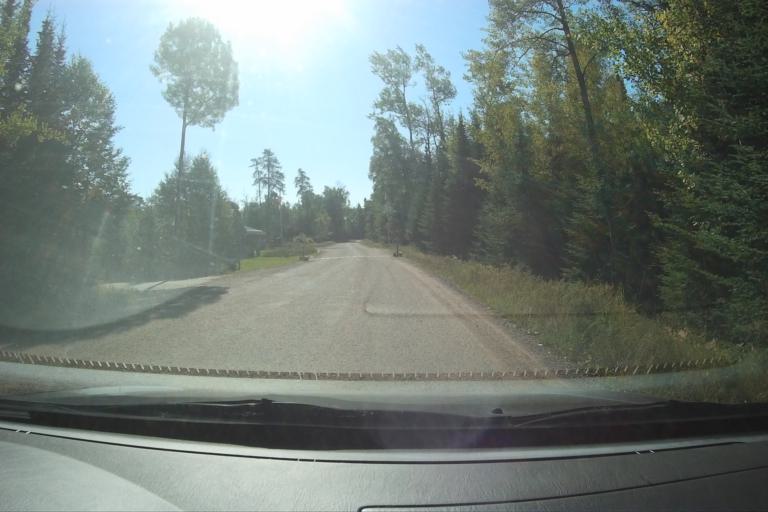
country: CA
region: Ontario
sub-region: Thunder Bay District
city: Thunder Bay
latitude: 48.3620
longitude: -88.8010
